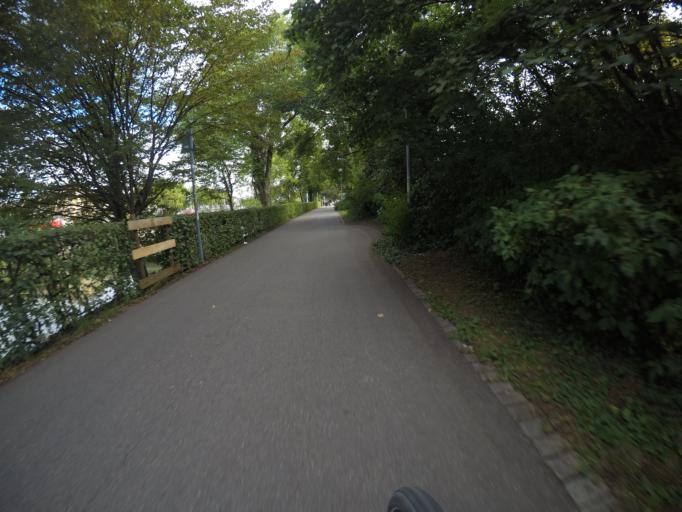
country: DE
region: Baden-Wuerttemberg
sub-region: Regierungsbezirk Stuttgart
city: Stuttgart-Ost
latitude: 48.8043
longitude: 9.2107
